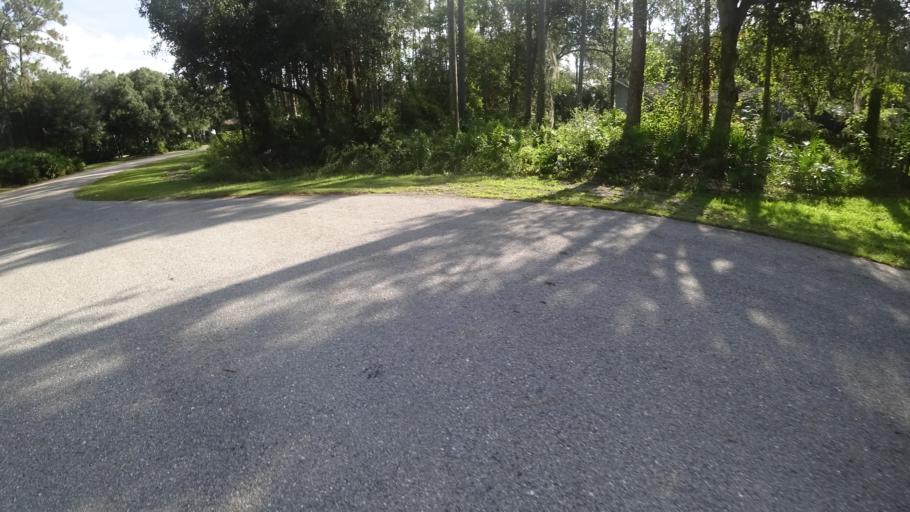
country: US
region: Florida
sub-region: Sarasota County
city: The Meadows
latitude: 27.4372
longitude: -82.4421
